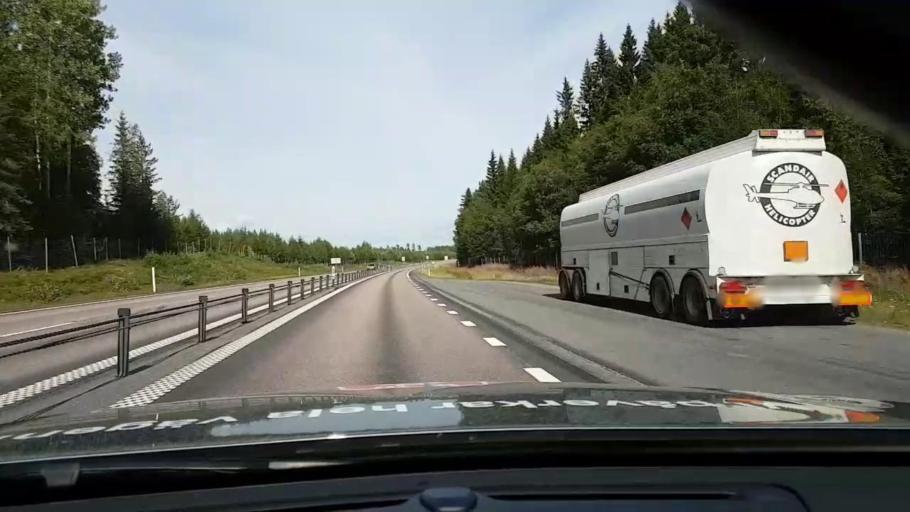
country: SE
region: Vaesternorrland
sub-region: OErnskoeldsviks Kommun
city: Husum
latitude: 63.4401
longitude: 19.2130
